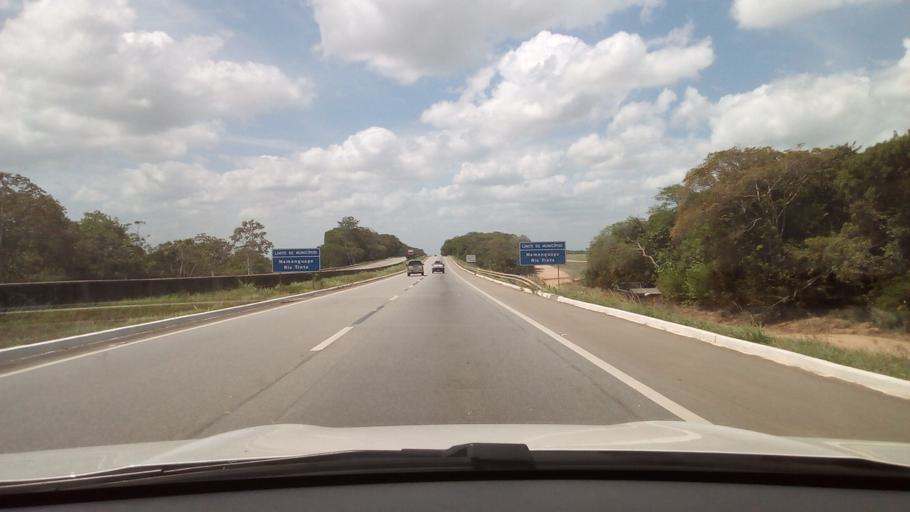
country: BR
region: Paraiba
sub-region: Mamanguape
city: Mamanguape
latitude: -6.8972
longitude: -35.1225
